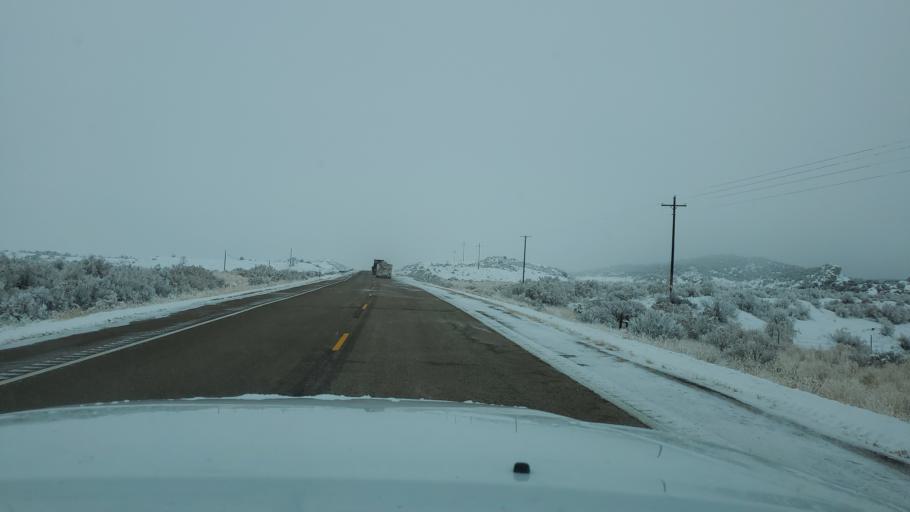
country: US
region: Colorado
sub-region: Rio Blanco County
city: Rangely
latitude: 40.2428
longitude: -108.9526
